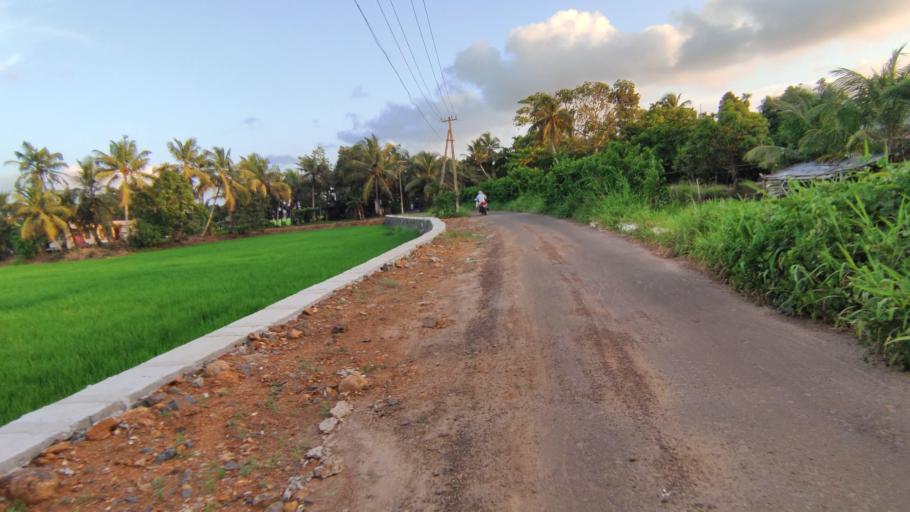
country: IN
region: Kerala
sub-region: Kottayam
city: Kottayam
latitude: 9.5841
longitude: 76.4480
